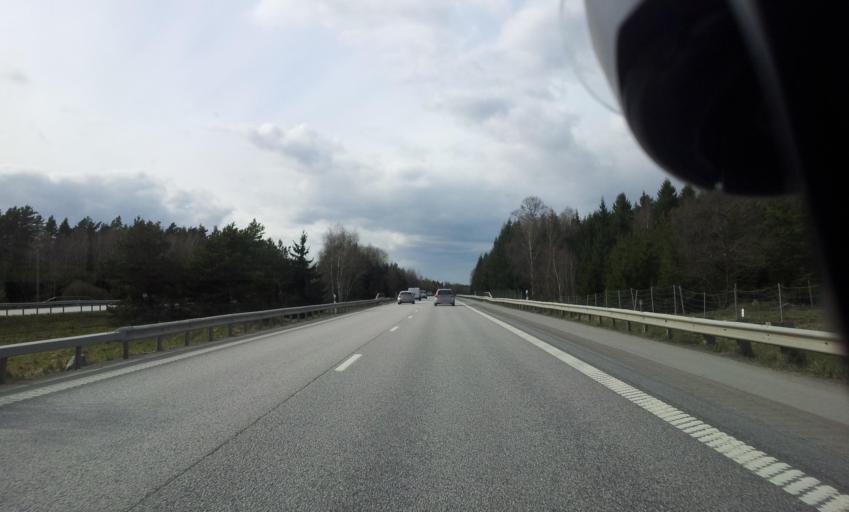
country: SE
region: Stockholm
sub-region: Upplands-Bro Kommun
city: Bro
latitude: 59.5410
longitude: 17.6129
